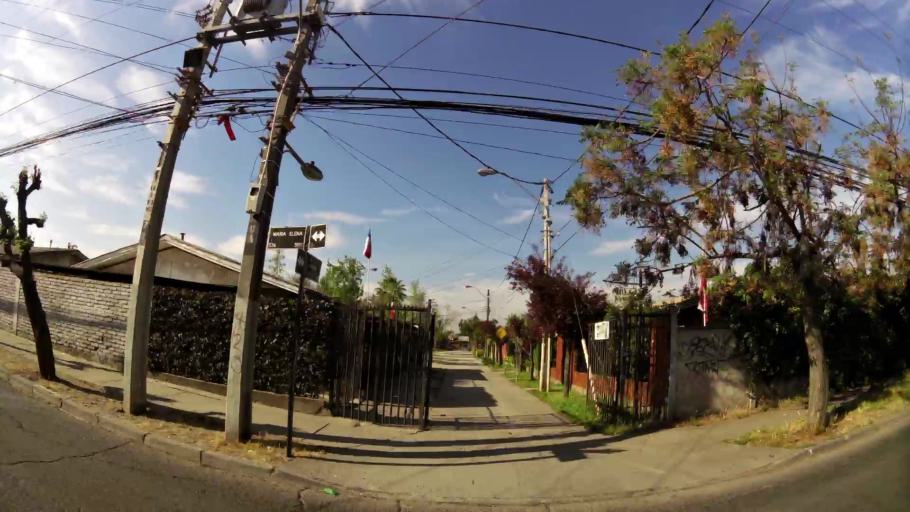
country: CL
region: Santiago Metropolitan
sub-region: Provincia de Santiago
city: La Pintana
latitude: -33.5616
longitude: -70.5934
